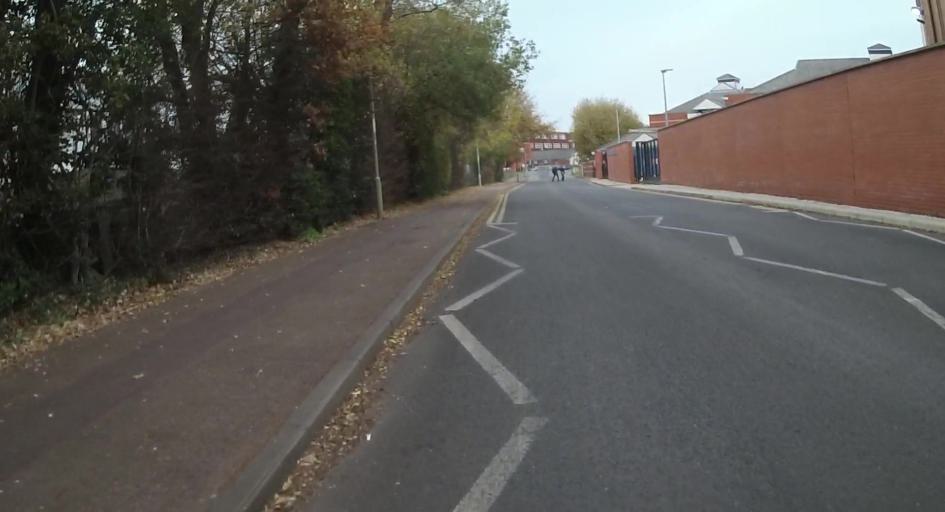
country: GB
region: England
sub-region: Hampshire
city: Farnborough
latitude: 51.2919
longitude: -0.7595
